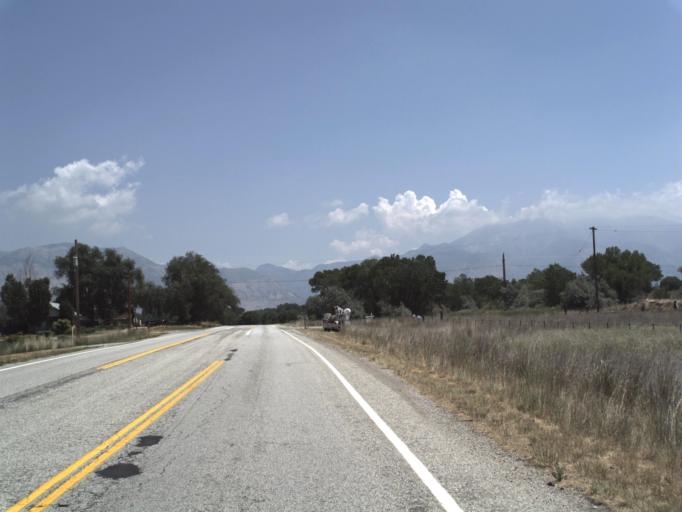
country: US
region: Utah
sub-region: Weber County
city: Marriott-Slaterville
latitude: 41.2444
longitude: -112.0515
